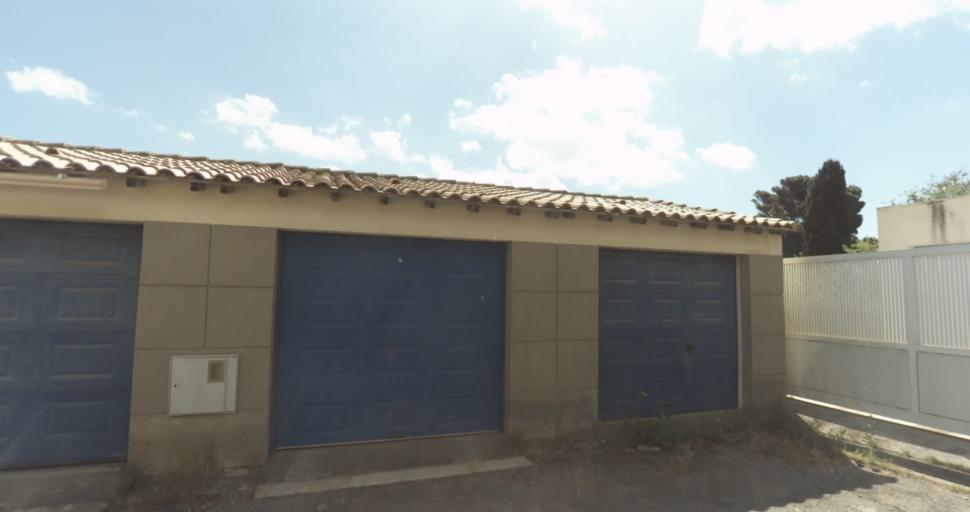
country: FR
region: Languedoc-Roussillon
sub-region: Departement de l'Aude
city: Leucate
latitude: 42.9050
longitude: 3.0529
